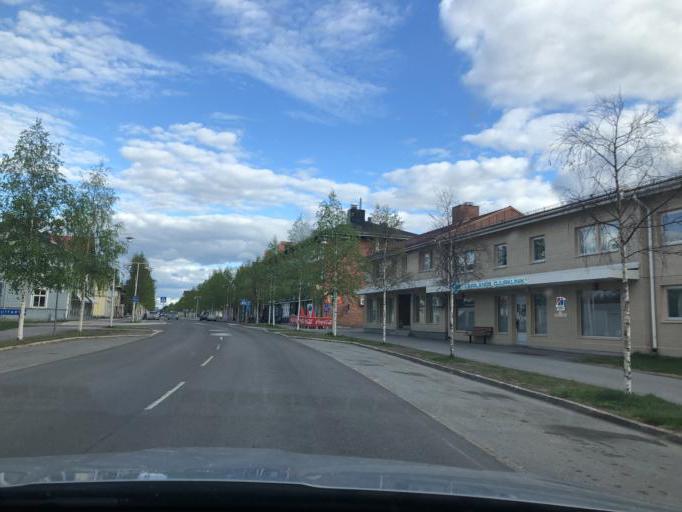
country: SE
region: Norrbotten
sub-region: Arvidsjaurs Kommun
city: Arvidsjaur
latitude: 65.5947
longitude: 19.1698
